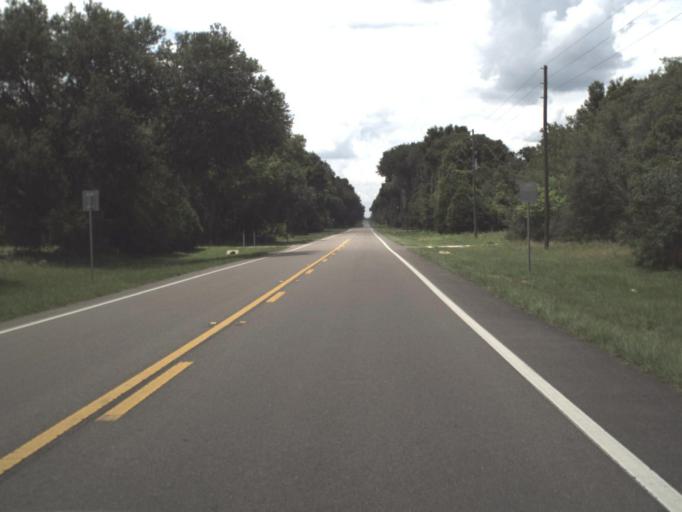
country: US
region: Florida
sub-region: Levy County
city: Williston
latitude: 29.4473
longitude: -82.4694
